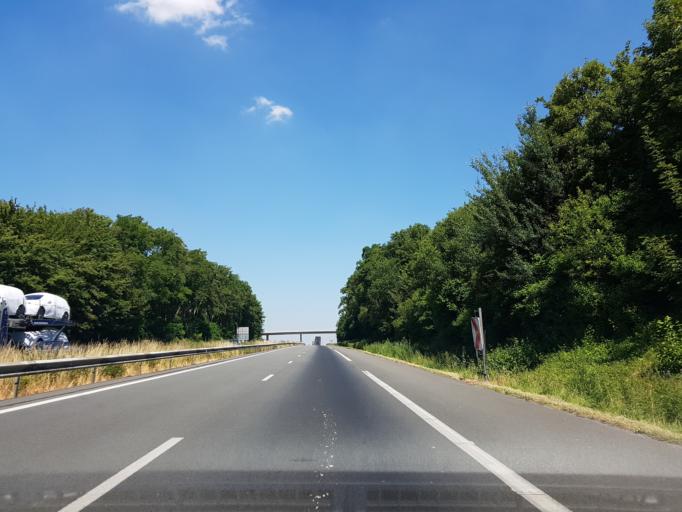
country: FR
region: Nord-Pas-de-Calais
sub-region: Departement du Nord
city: Marcoing
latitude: 50.0903
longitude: 3.1711
